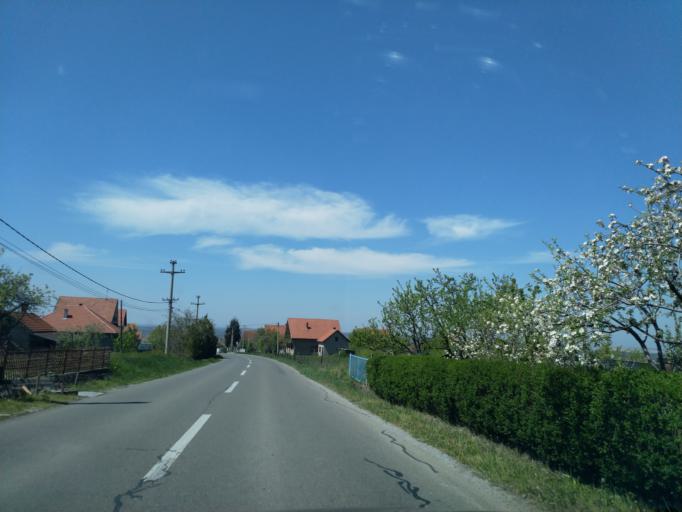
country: RS
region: Central Serbia
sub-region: Belgrade
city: Lazarevac
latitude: 44.3743
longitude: 20.2961
